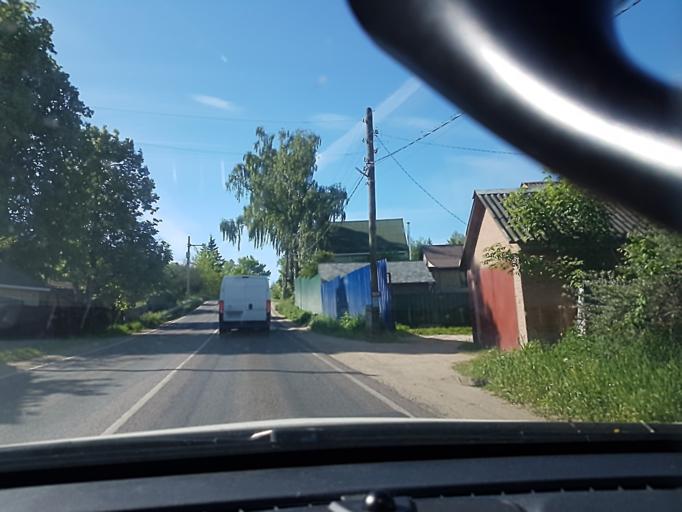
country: RU
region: Moskovskaya
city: Istra
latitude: 55.8902
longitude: 36.7964
